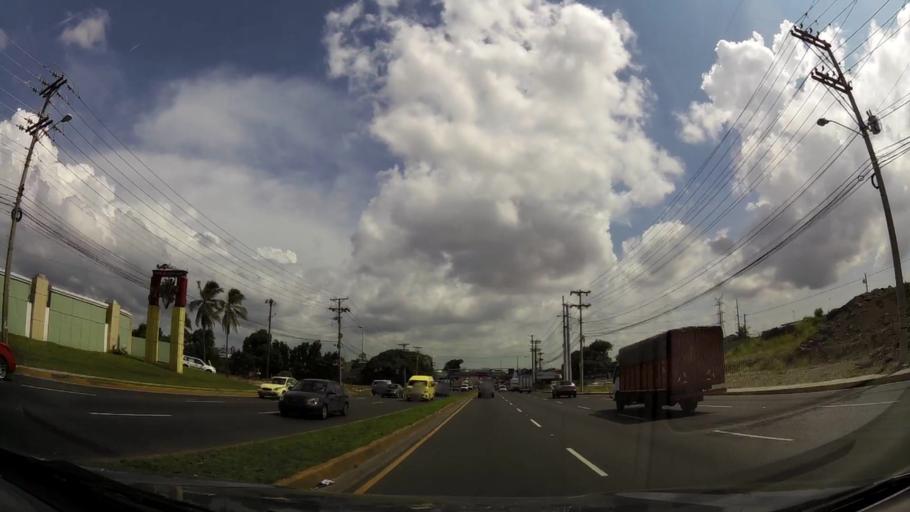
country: PA
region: Panama
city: San Miguelito
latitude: 9.0479
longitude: -79.4627
